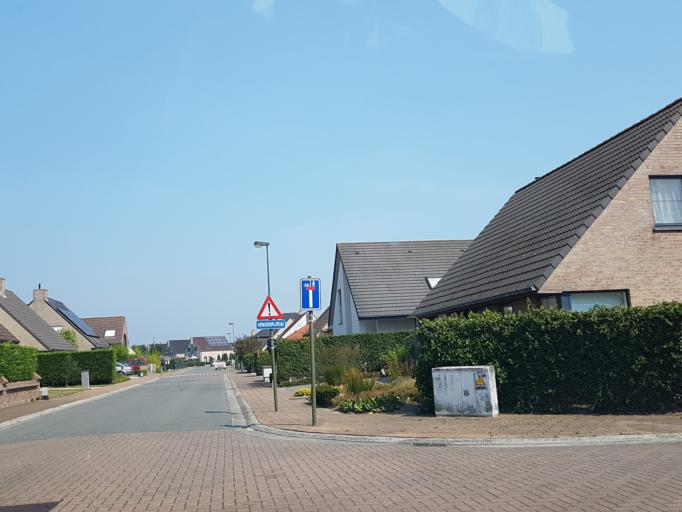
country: BE
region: Flanders
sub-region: Provincie West-Vlaanderen
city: Bredene
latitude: 51.2366
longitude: 2.9494
